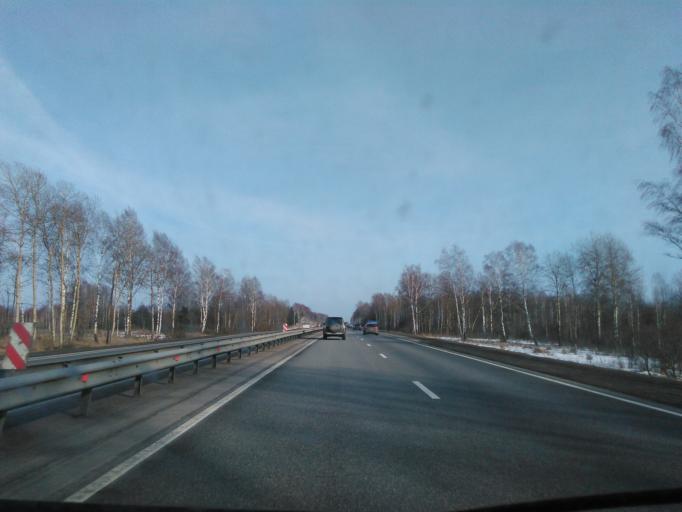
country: RU
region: Smolensk
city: Verkhnedneprovskiy
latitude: 55.1815
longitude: 33.5855
